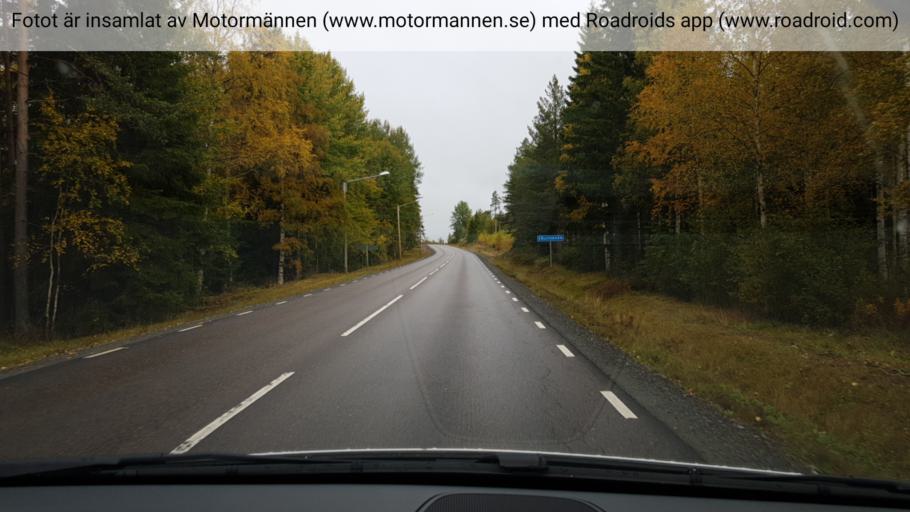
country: SE
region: Vaesterbotten
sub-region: Umea Kommun
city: Ersmark
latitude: 63.9250
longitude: 20.3025
